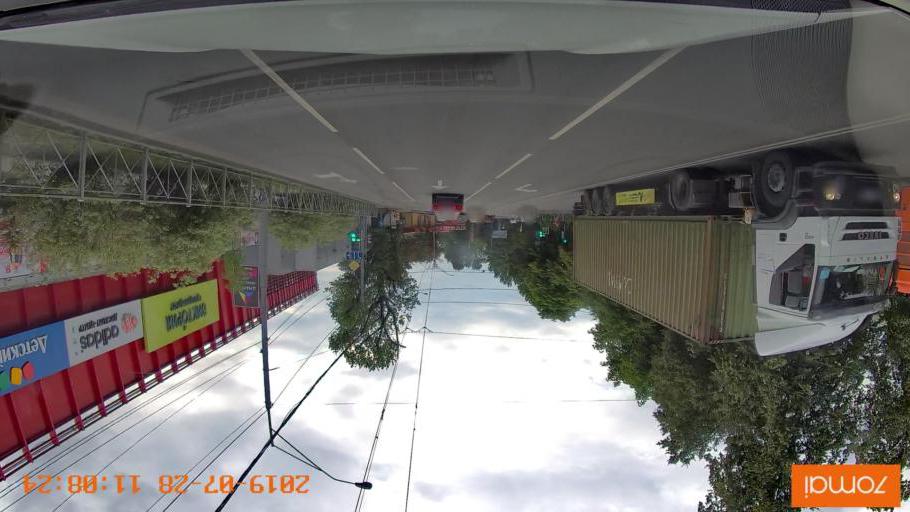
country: RU
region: Kaliningrad
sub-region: Gorod Kaliningrad
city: Kaliningrad
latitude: 54.7106
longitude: 20.4421
